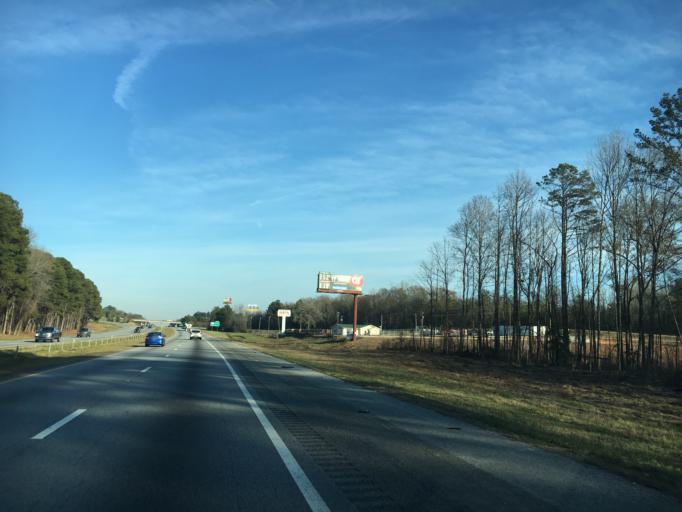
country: US
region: Georgia
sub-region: Hart County
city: Reed Creek
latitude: 34.5042
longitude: -82.9717
